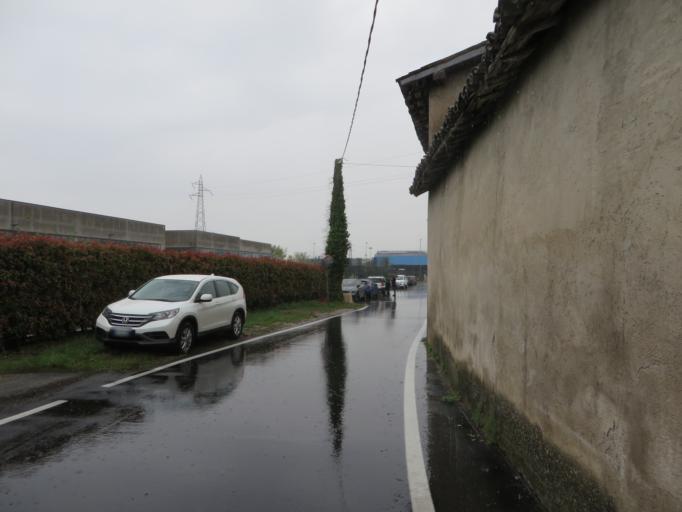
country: IT
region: Lombardy
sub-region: Provincia di Brescia
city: Lonato
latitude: 45.4590
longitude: 10.4642
